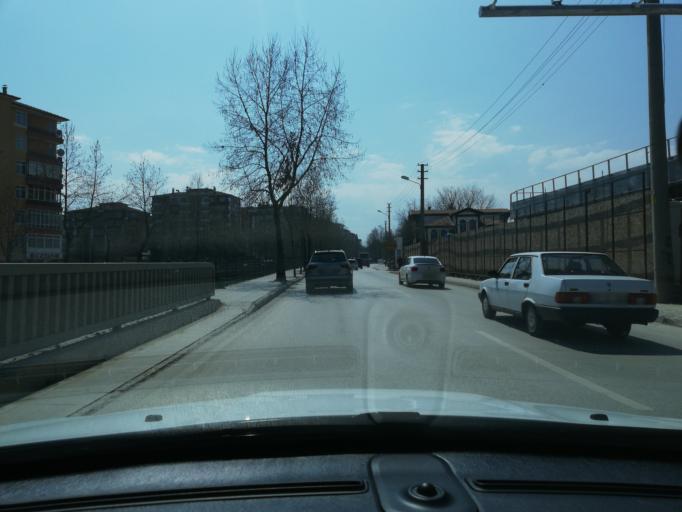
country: TR
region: Kastamonu
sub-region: Cide
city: Kastamonu
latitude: 41.3914
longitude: 33.7814
